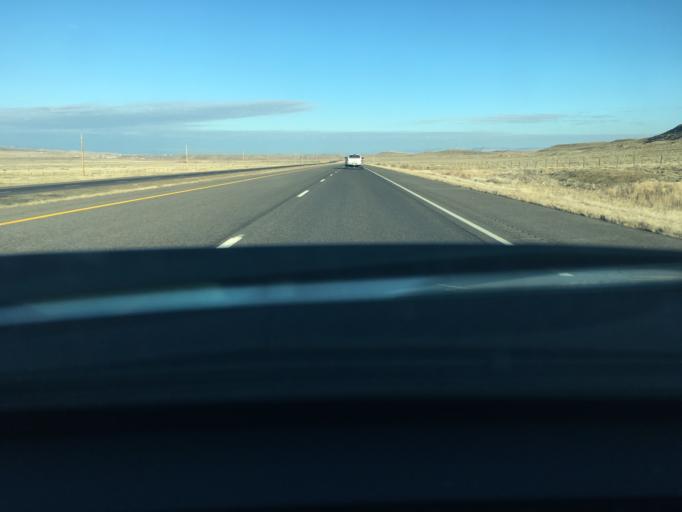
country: US
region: Colorado
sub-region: Mesa County
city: Clifton
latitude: 38.8972
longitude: -108.3647
